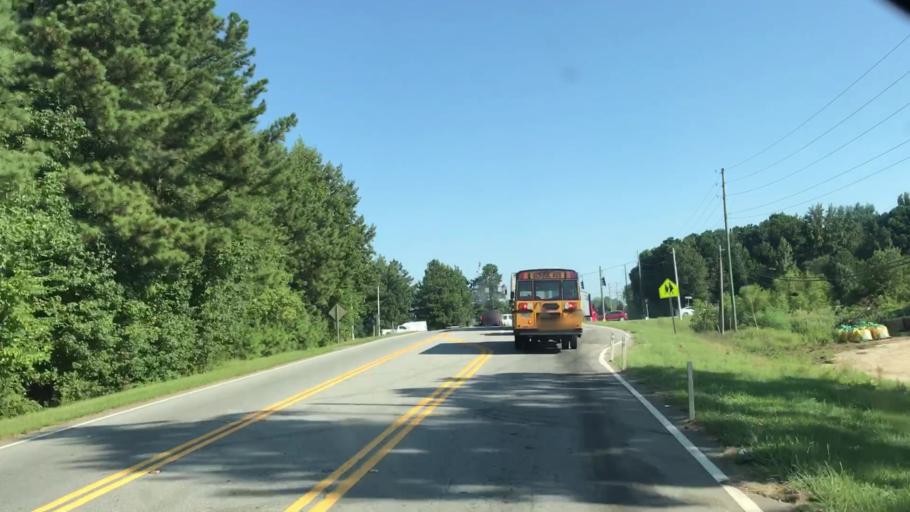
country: US
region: Georgia
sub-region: Gwinnett County
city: Lawrenceville
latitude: 33.9805
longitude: -83.9725
